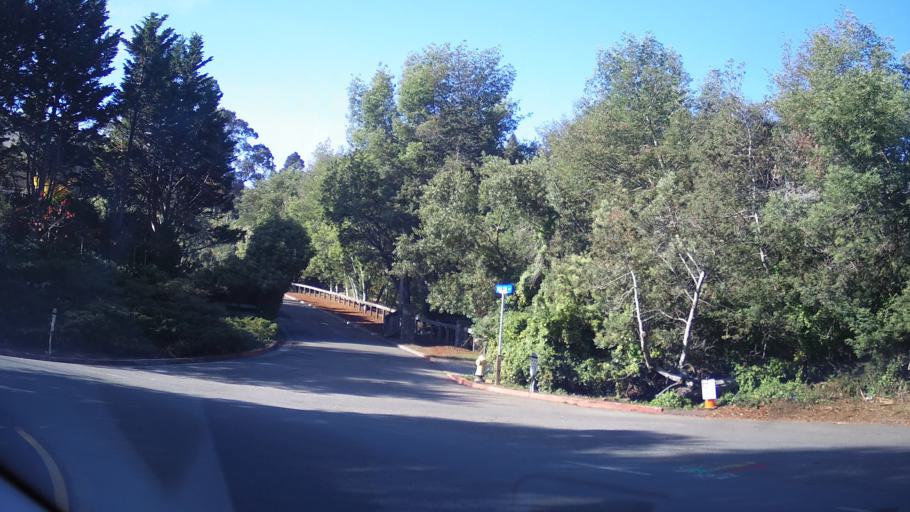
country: US
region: California
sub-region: Marin County
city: Mill Valley
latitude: 37.9022
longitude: -122.5584
